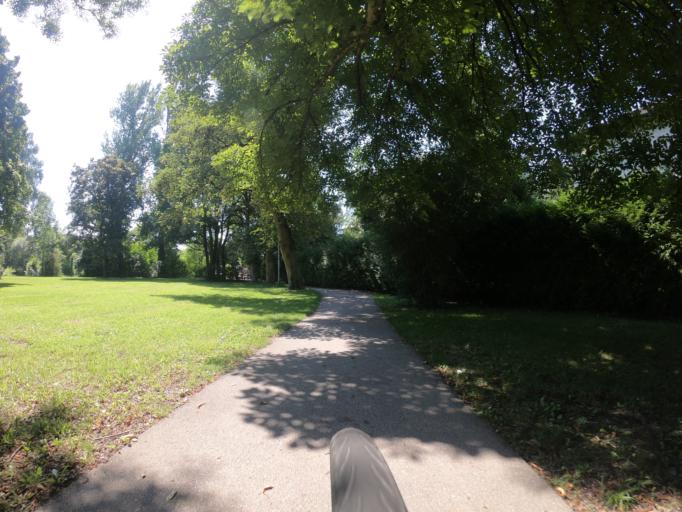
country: DE
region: Bavaria
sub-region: Upper Bavaria
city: Fuerstenfeldbruck
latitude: 48.1778
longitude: 11.2611
